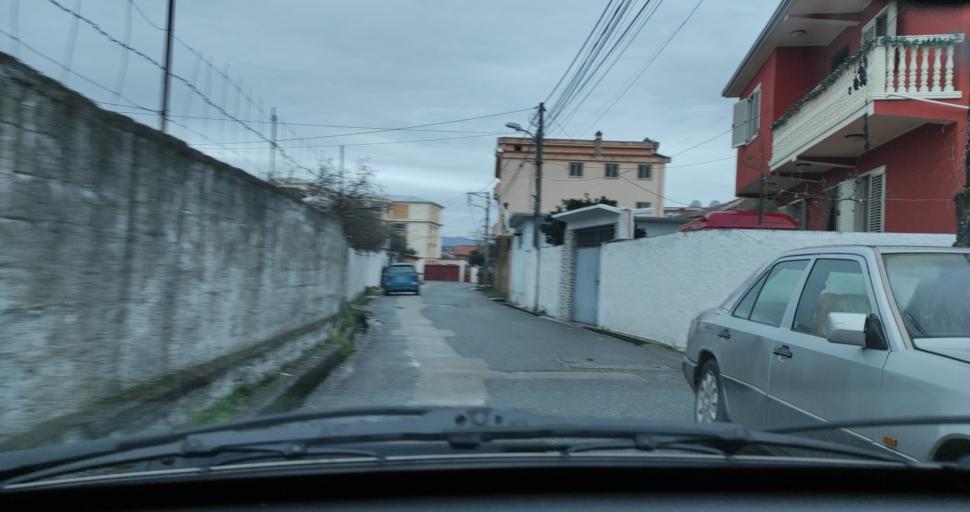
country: AL
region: Shkoder
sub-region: Rrethi i Shkodres
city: Shkoder
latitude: 42.0770
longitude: 19.5095
